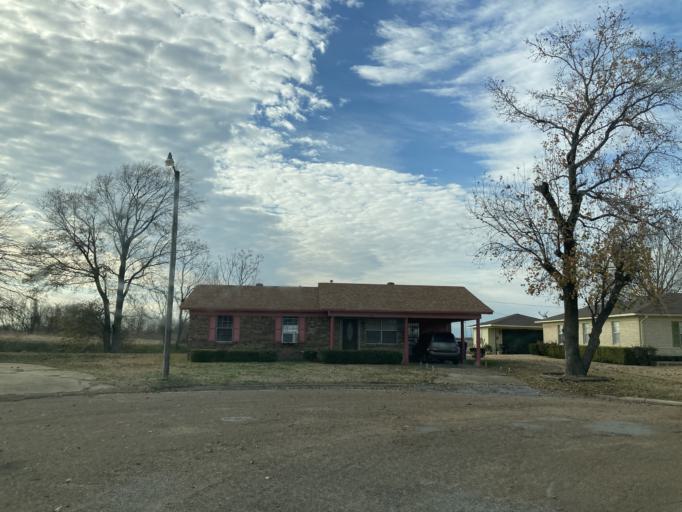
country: US
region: Mississippi
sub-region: Humphreys County
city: Belzoni
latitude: 33.1681
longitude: -90.5032
